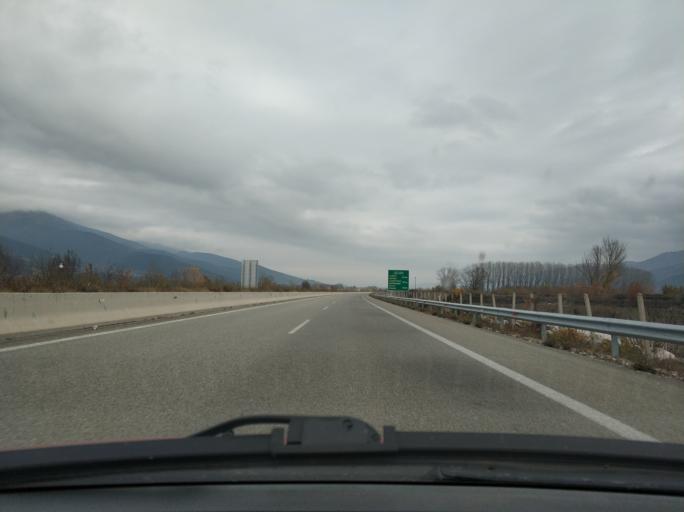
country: GR
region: East Macedonia and Thrace
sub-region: Nomos Kavalas
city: Nikisiani
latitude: 40.8443
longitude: 24.1231
